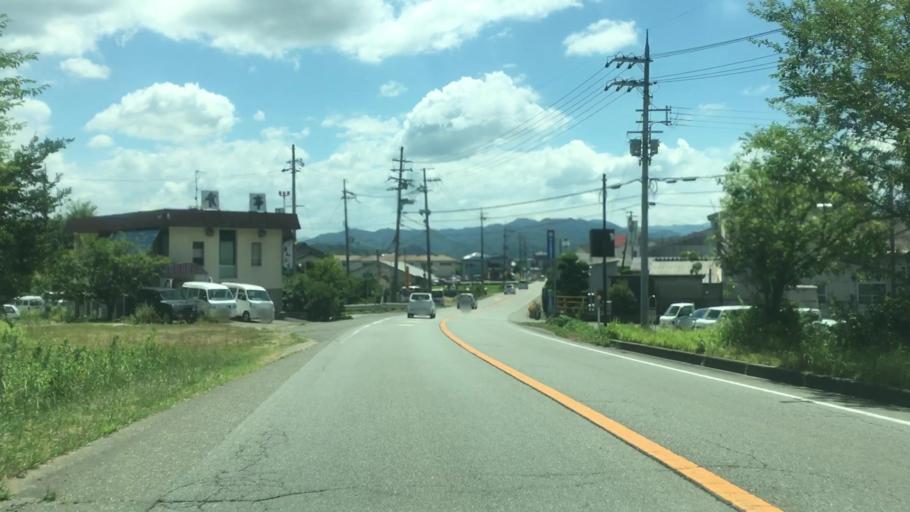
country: JP
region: Hyogo
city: Toyooka
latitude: 35.4997
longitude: 134.8059
